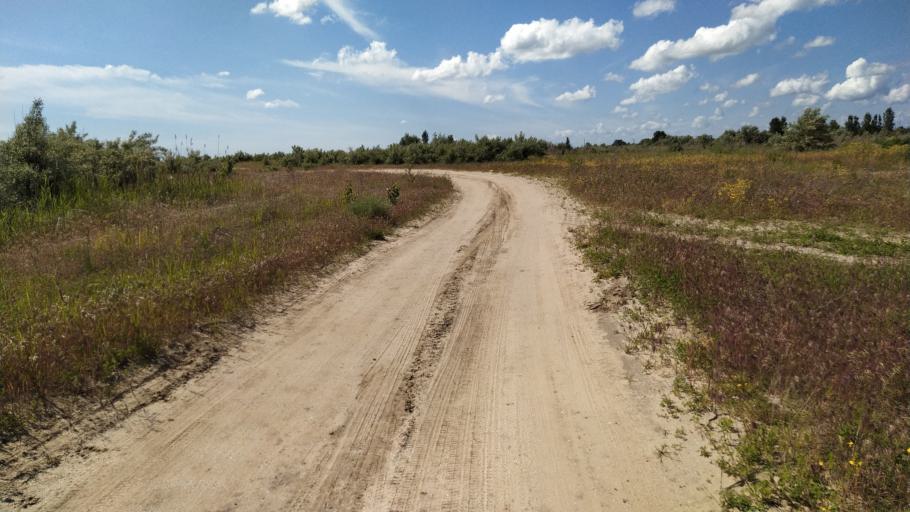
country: RU
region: Rostov
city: Bataysk
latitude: 47.1454
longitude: 39.6697
